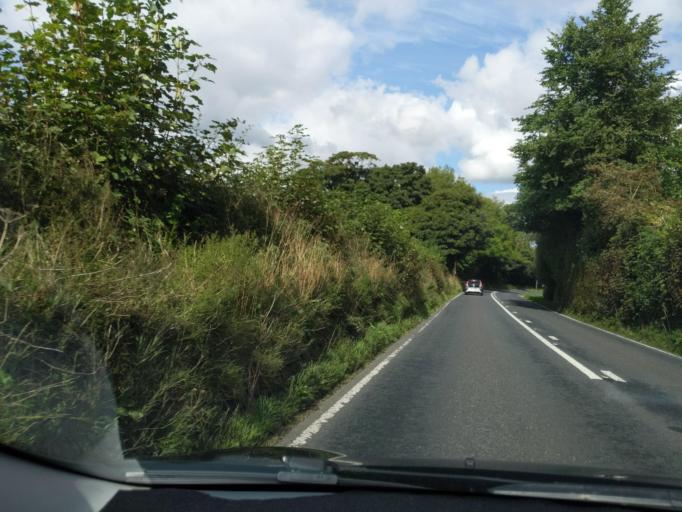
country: GB
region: England
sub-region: Cornwall
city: South Hill
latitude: 50.5519
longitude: -4.3325
